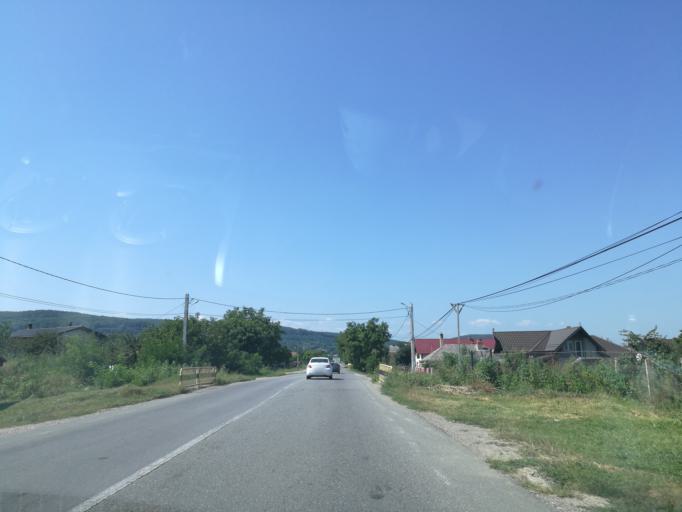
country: RO
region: Bacau
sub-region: Comuna Garleni
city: Garleni
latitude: 46.6614
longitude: 26.7855
